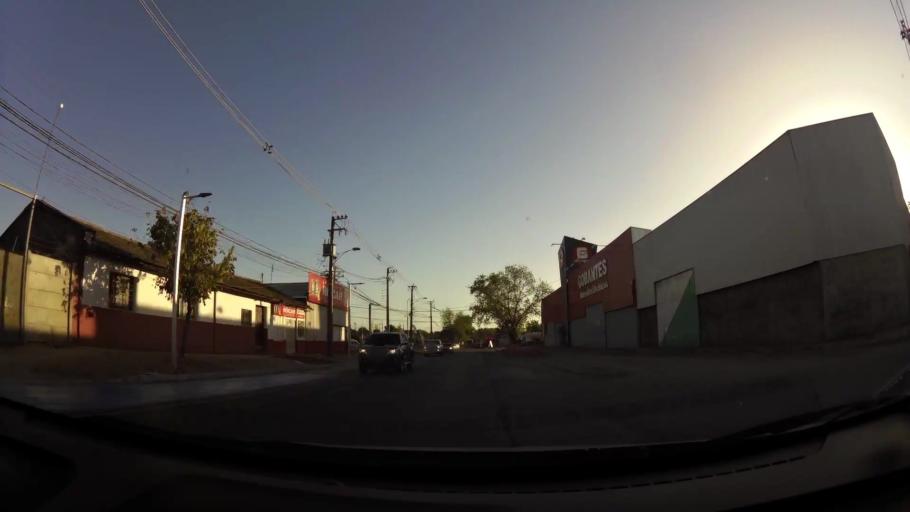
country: CL
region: Maule
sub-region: Provincia de Talca
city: Talca
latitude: -35.4361
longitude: -71.6436
